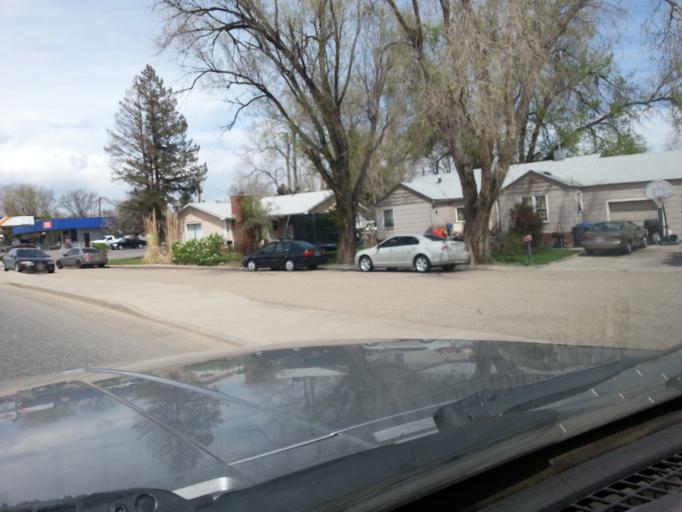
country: US
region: Colorado
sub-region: Larimer County
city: Loveland
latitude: 40.4070
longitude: -105.0942
